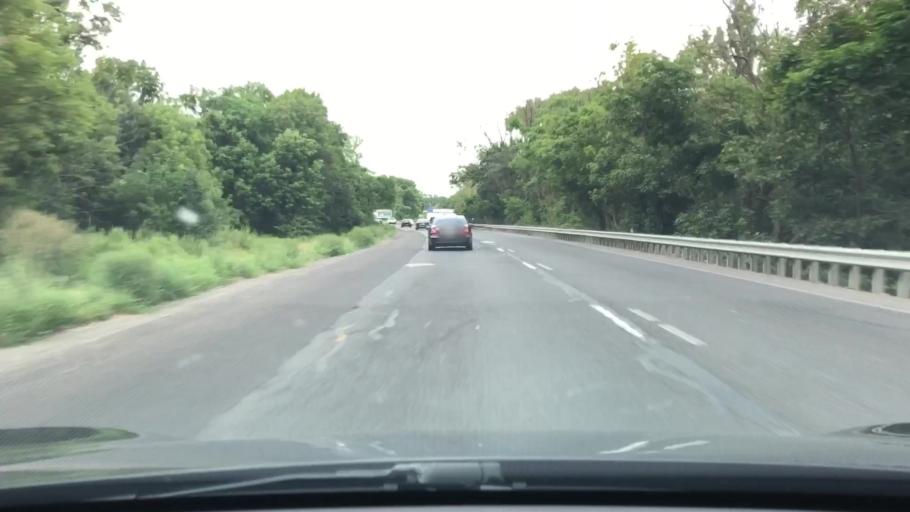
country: US
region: Pennsylvania
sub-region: Bucks County
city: Morrisville
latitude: 40.1976
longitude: -74.7914
